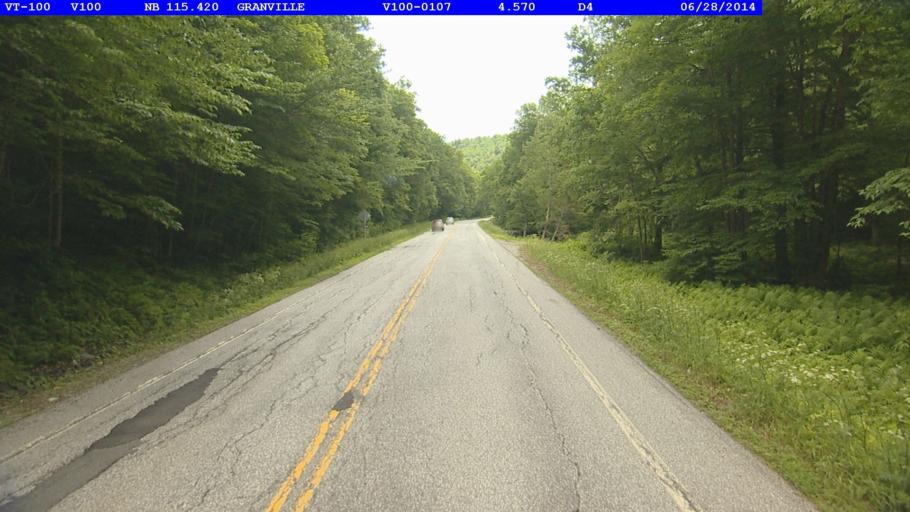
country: US
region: Vermont
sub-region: Orange County
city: Randolph
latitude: 44.0048
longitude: -72.8489
